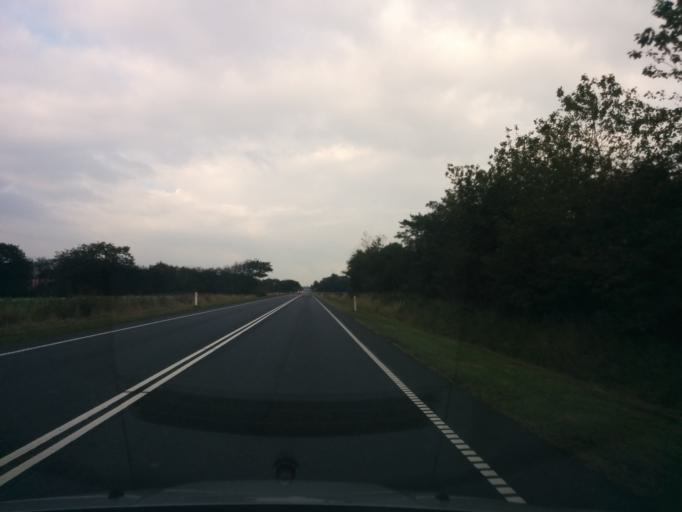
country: DK
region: South Denmark
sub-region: Esbjerg Kommune
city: Bramming
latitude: 55.6174
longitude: 8.7545
